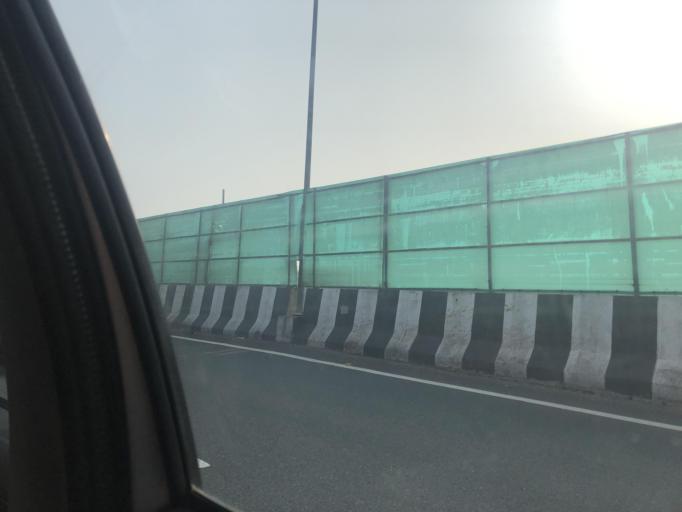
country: IN
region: NCT
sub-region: Central Delhi
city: Karol Bagh
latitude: 28.5911
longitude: 77.1586
